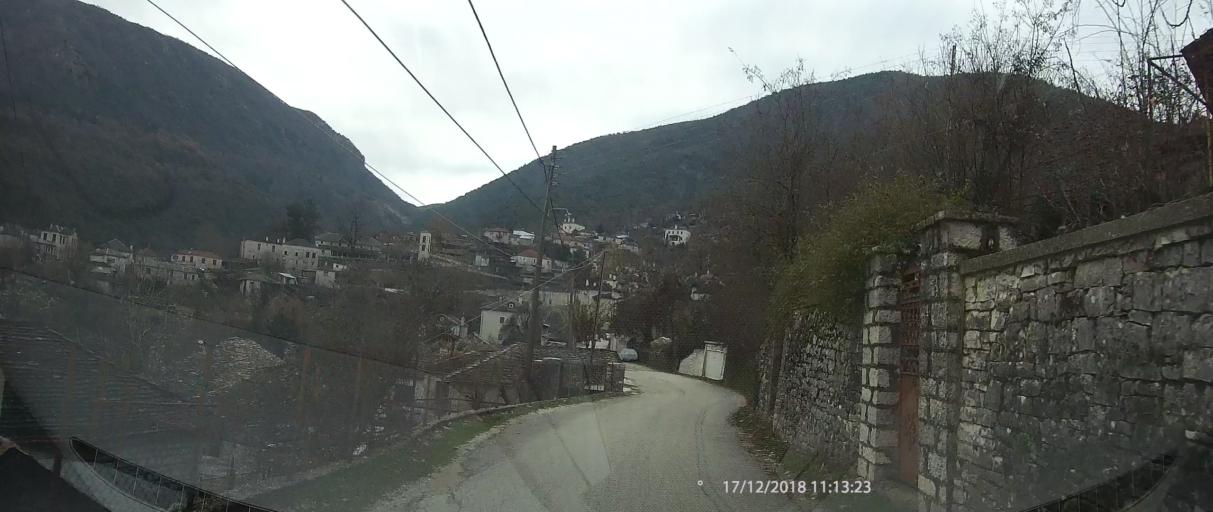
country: GR
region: Epirus
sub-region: Nomos Ioanninon
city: Kalpaki
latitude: 39.9359
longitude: 20.6728
